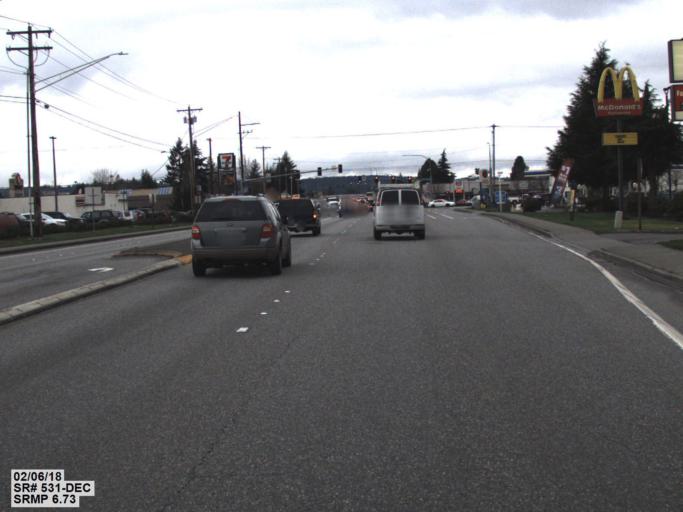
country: US
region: Washington
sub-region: Snohomish County
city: Smokey Point
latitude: 48.1525
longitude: -122.1808
